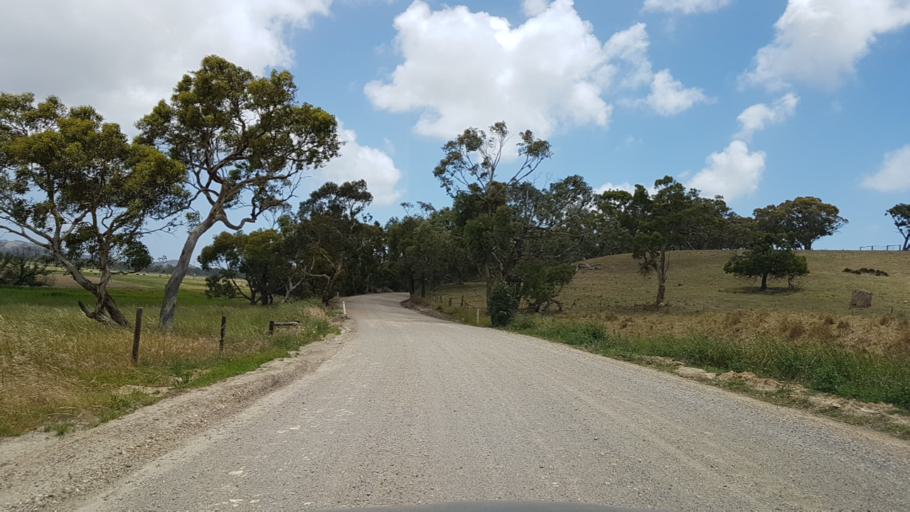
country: AU
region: South Australia
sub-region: Onkaparinga
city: Aldinga
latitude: -35.3747
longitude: 138.5096
